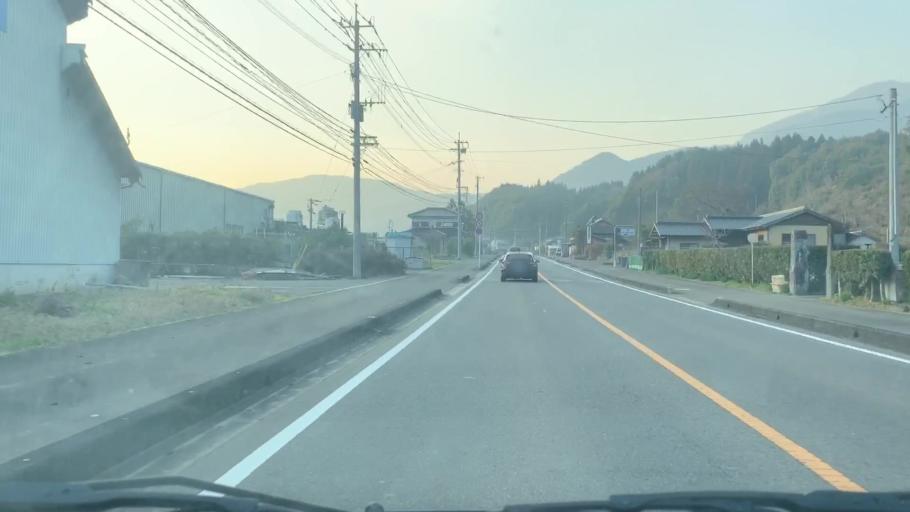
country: JP
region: Saga Prefecture
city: Takeocho-takeo
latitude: 33.2634
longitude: 130.0556
